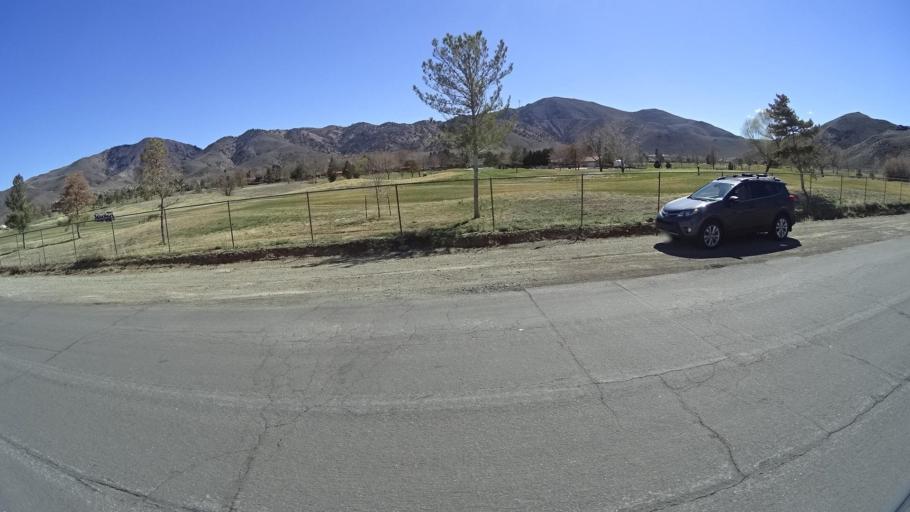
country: US
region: Nevada
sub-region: Washoe County
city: Sparks
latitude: 39.4856
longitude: -119.7299
